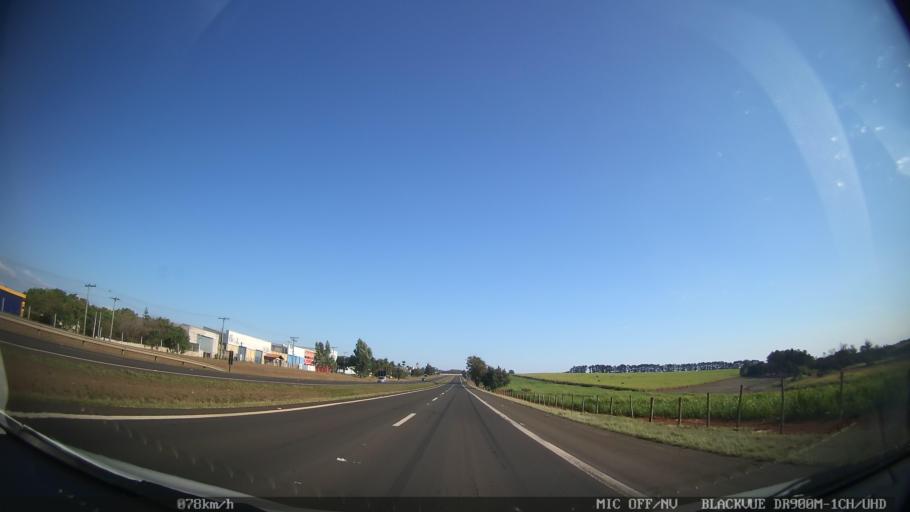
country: BR
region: Sao Paulo
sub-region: Piracicaba
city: Piracicaba
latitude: -22.6821
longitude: -47.6368
